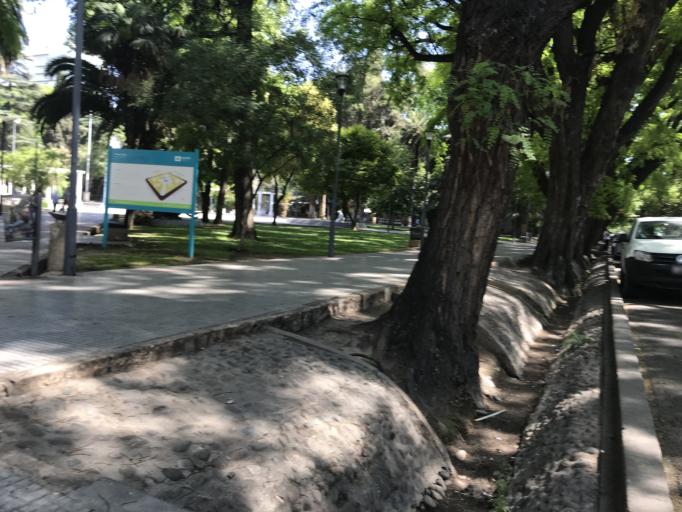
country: AR
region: Mendoza
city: Mendoza
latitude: -32.8923
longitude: -68.8480
